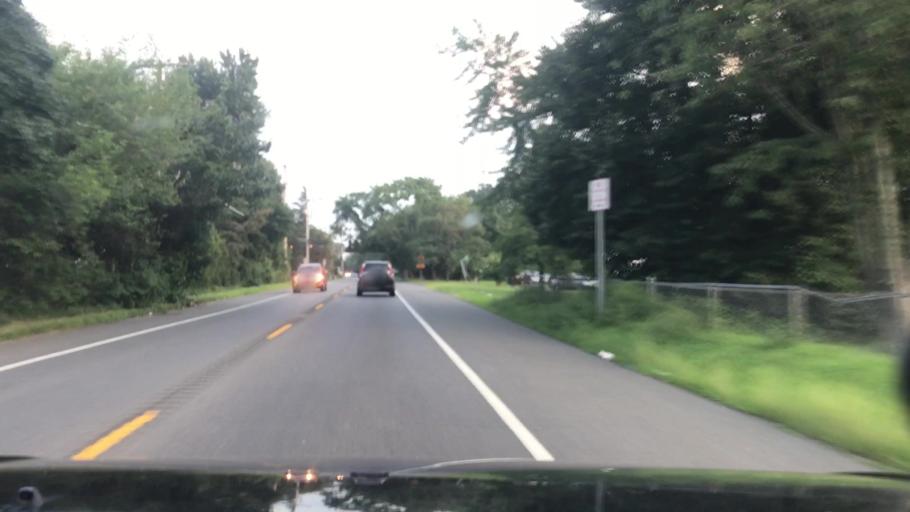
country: US
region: New Jersey
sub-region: Ocean County
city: Silver Ridge
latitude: 39.9797
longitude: -74.2090
